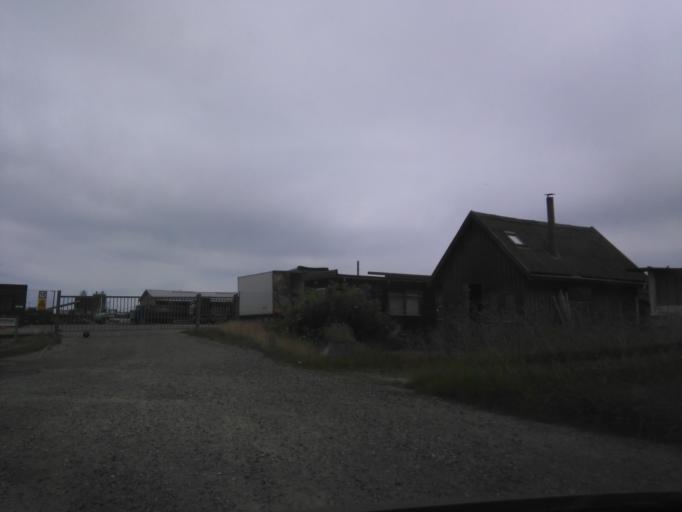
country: DK
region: Central Jutland
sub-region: Horsens Kommune
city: Horsens
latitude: 55.8538
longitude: 9.8700
